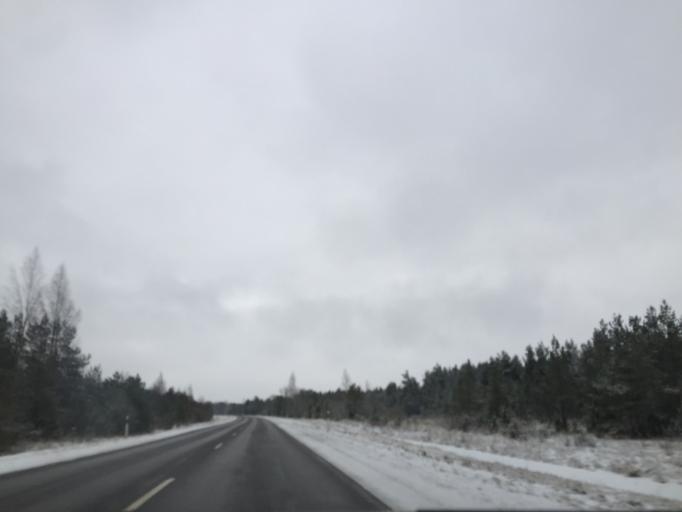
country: EE
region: Laeaene
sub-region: Lihula vald
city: Lihula
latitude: 58.6143
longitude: 23.9183
